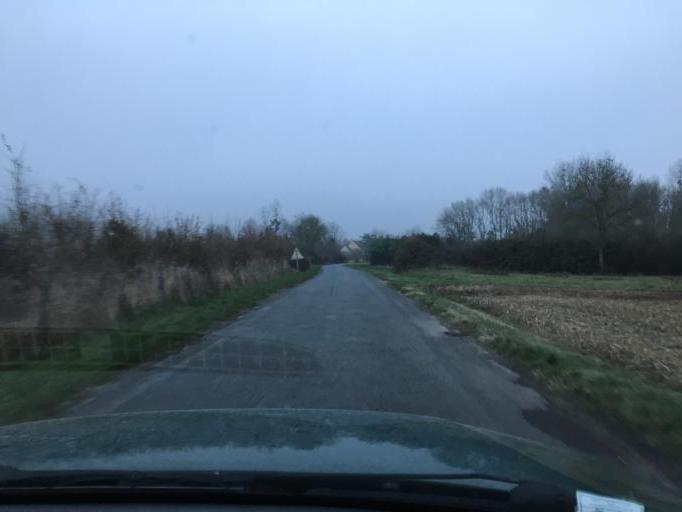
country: FR
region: Centre
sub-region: Departement du Loiret
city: Lailly-en-Val
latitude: 47.7608
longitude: 1.6693
